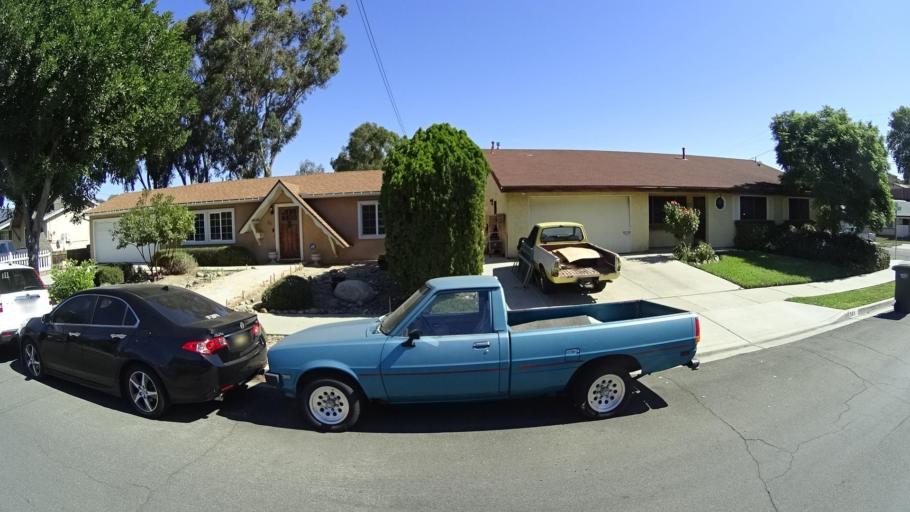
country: US
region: California
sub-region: San Diego County
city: La Presa
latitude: 32.7027
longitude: -117.0164
